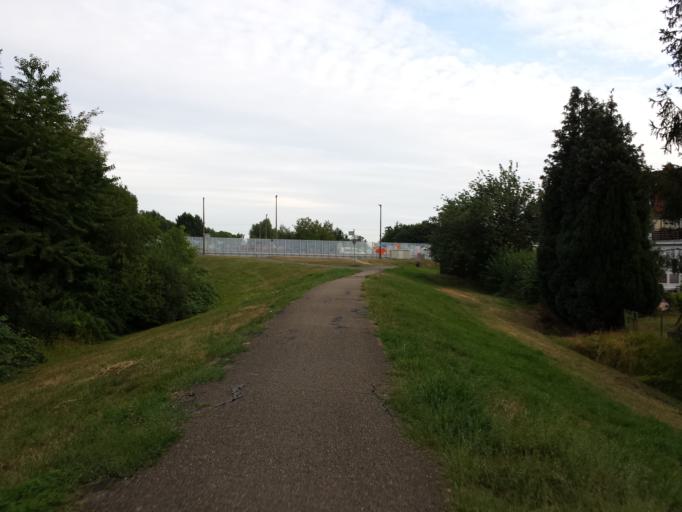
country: DE
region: Lower Saxony
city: Stuhr
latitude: 53.0622
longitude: 8.7681
